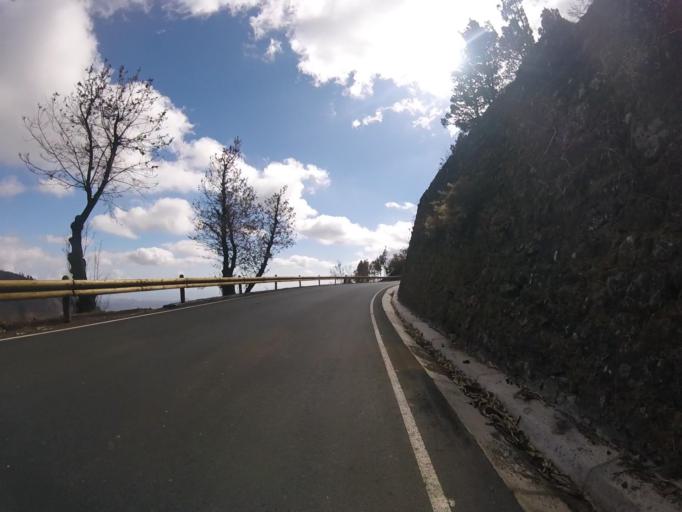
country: ES
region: Canary Islands
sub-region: Provincia de Las Palmas
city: Tejeda
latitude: 28.0033
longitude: -15.5955
